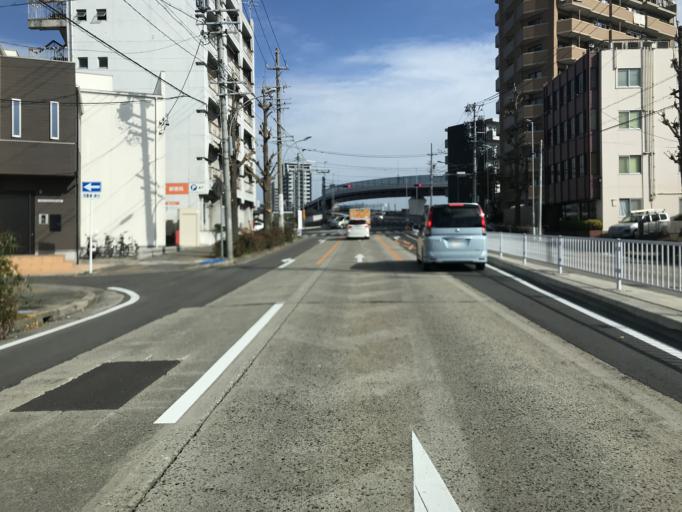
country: JP
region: Aichi
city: Nagoya-shi
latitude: 35.2070
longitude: 136.9281
